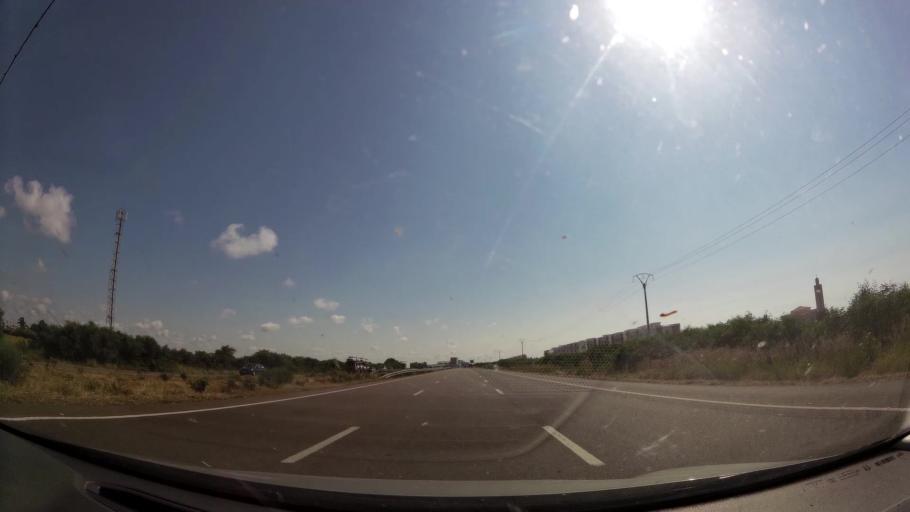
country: MA
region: Chaouia-Ouardigha
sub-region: Benslimane
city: Bouznika
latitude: 33.8112
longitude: -7.1386
